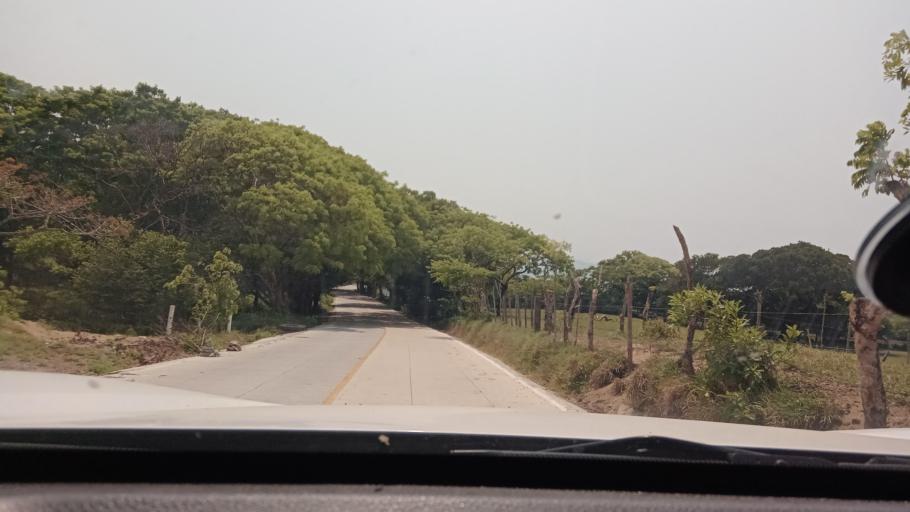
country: MX
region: Veracruz
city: Catemaco
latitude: 18.5578
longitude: -95.0133
